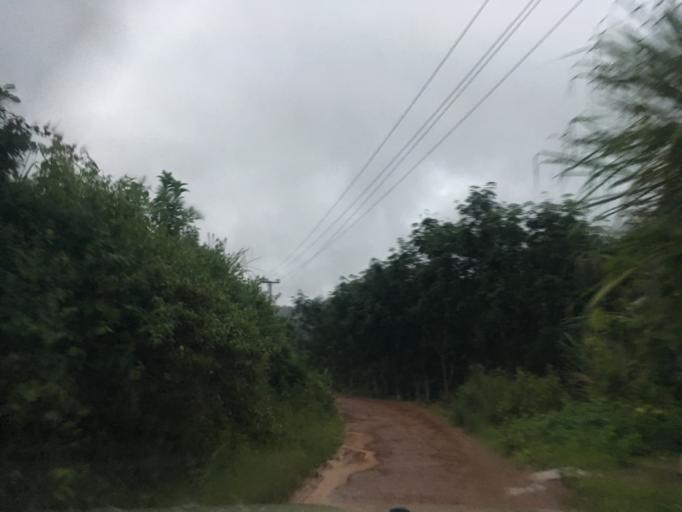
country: LA
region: Oudomxai
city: Muang La
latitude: 21.2537
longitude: 101.9321
